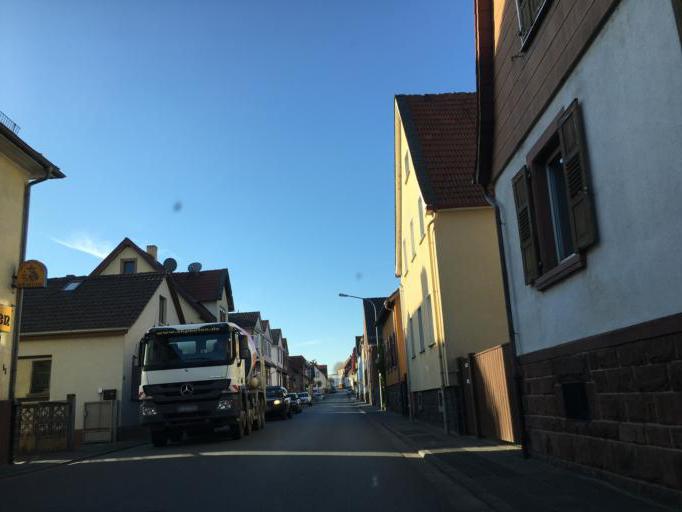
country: DE
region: Hesse
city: Reinheim
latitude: 49.8275
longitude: 8.8379
